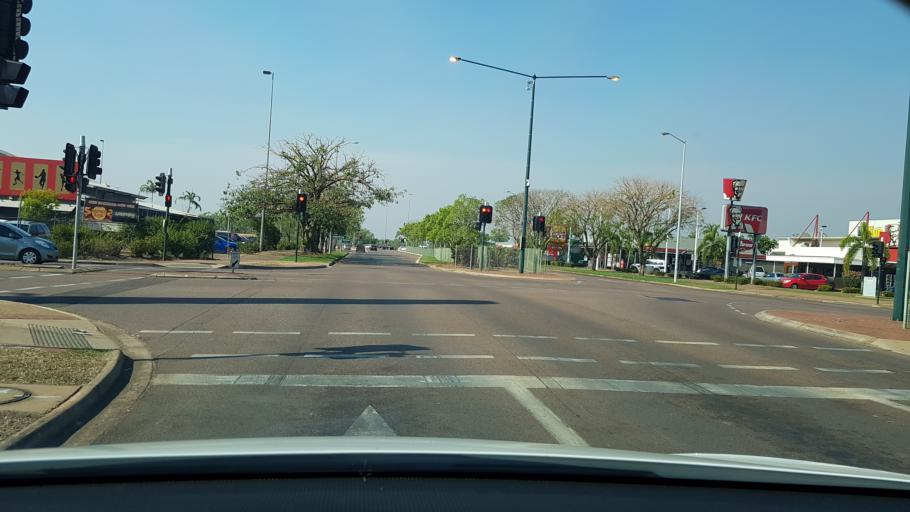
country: AU
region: Northern Territory
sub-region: Palmerston
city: Palmerston
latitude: -12.4808
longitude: 130.9866
